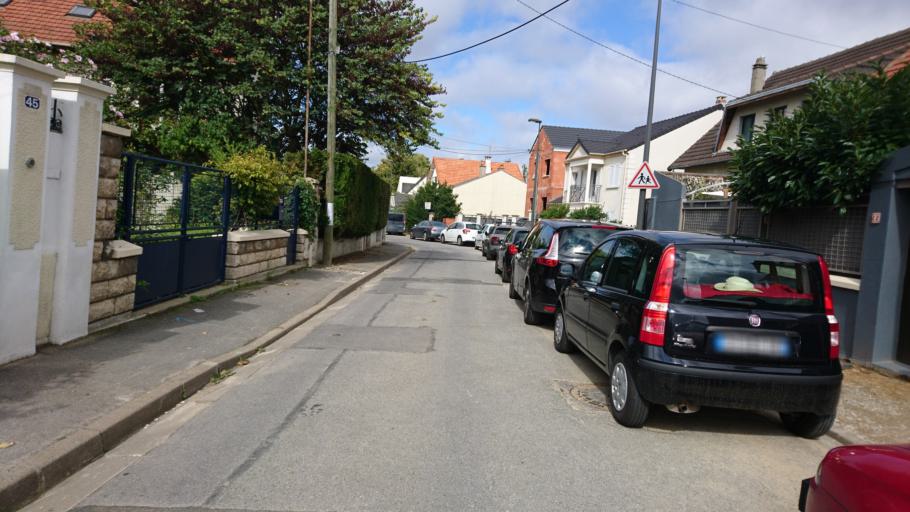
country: FR
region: Ile-de-France
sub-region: Departement des Hauts-de-Seine
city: Chatillon
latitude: 48.8041
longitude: 2.2811
